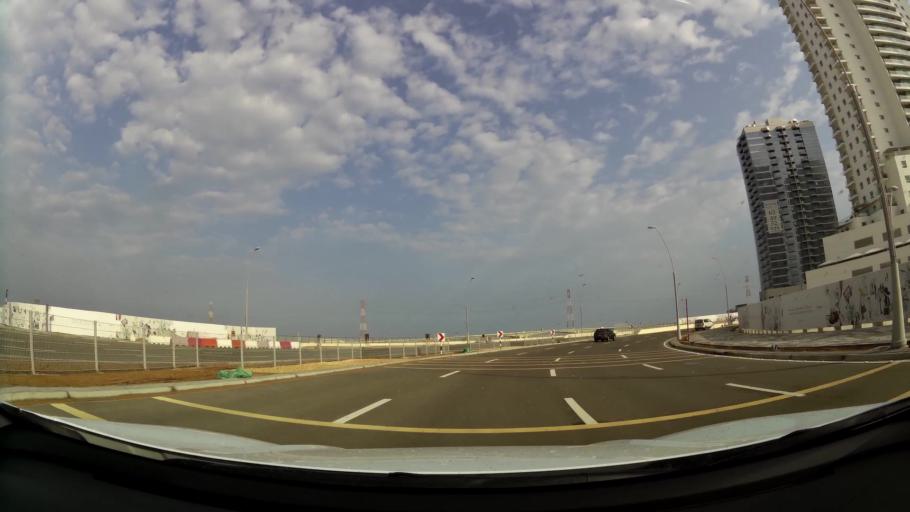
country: AE
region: Abu Dhabi
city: Abu Dhabi
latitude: 24.5103
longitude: 54.4047
